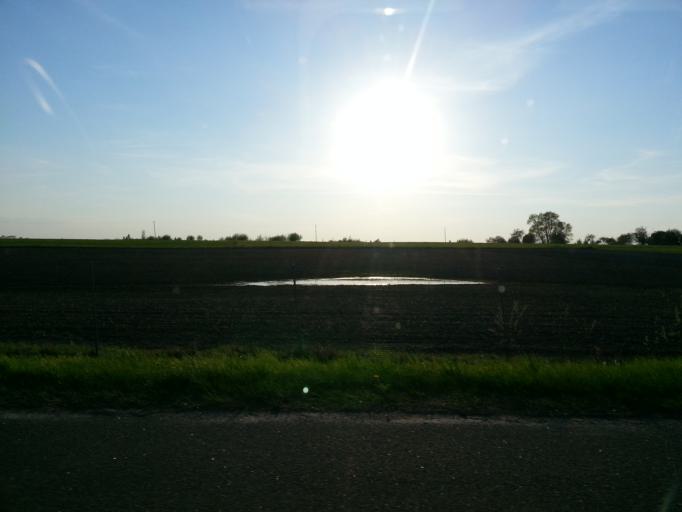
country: LT
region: Vilnius County
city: Ukmerge
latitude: 55.1992
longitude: 24.8142
